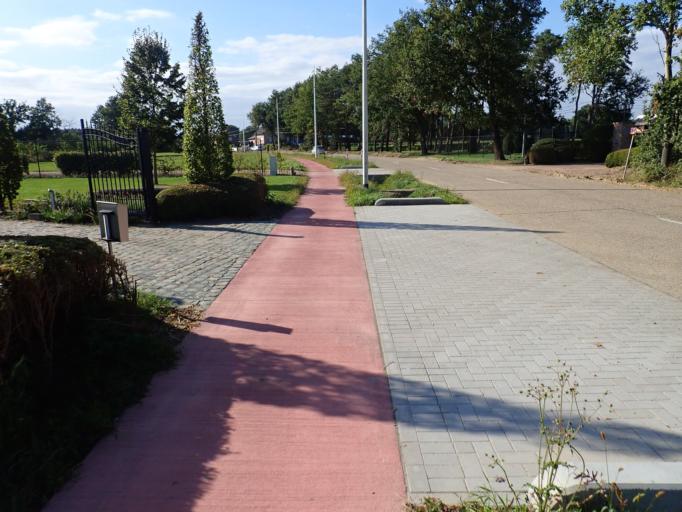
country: BE
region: Flanders
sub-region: Provincie Antwerpen
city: Nijlen
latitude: 51.1507
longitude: 4.6966
